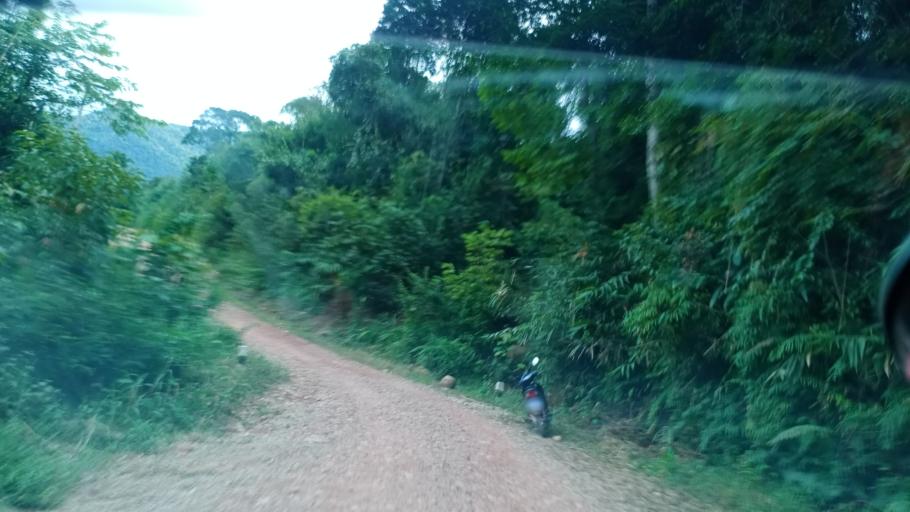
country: TH
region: Changwat Bueng Kan
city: Pak Khat
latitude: 18.7229
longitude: 103.2467
